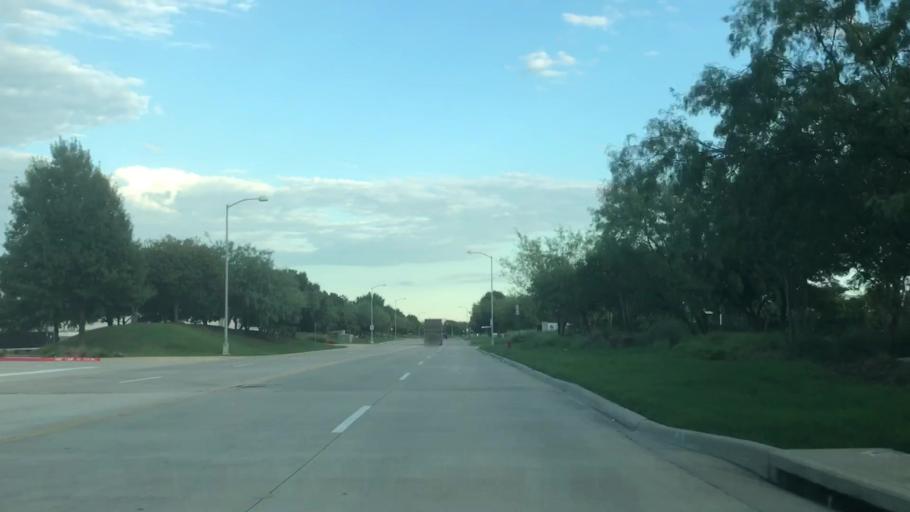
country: US
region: Texas
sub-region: Dallas County
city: Coppell
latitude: 32.9430
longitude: -97.0297
